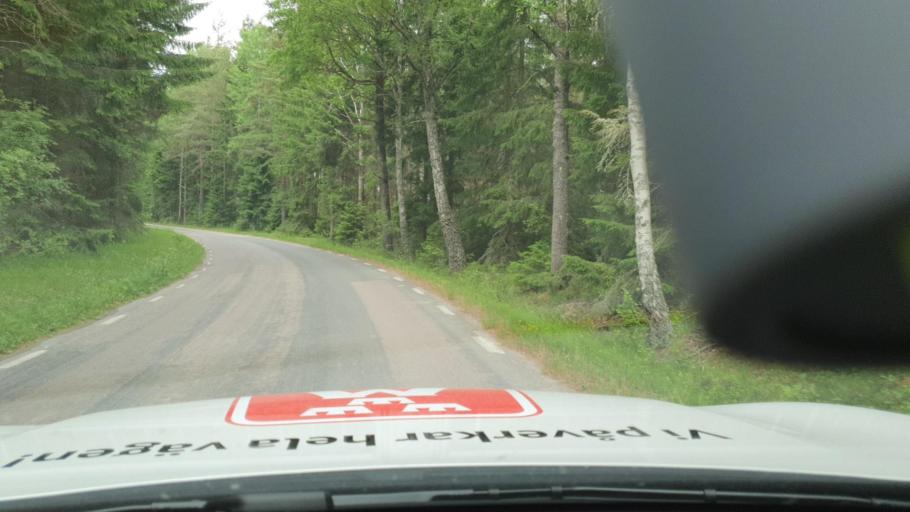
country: SE
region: Vaestra Goetaland
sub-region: Tidaholms Kommun
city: Tidaholm
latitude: 58.1770
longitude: 14.0110
